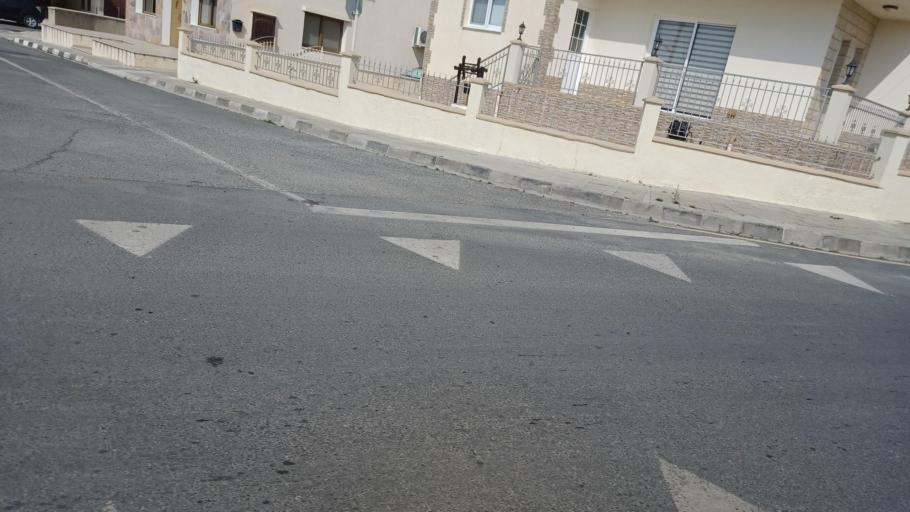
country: CY
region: Larnaka
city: Aradippou
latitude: 34.9295
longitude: 33.5356
